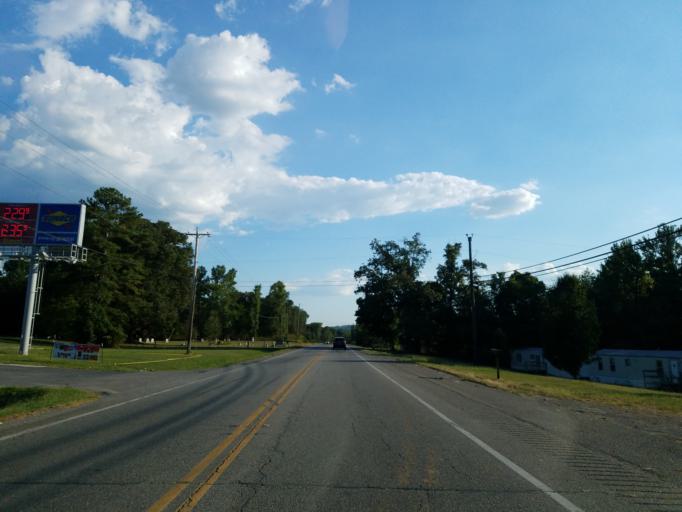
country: US
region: Georgia
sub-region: Murray County
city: Chatsworth
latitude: 34.8621
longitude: -84.7531
